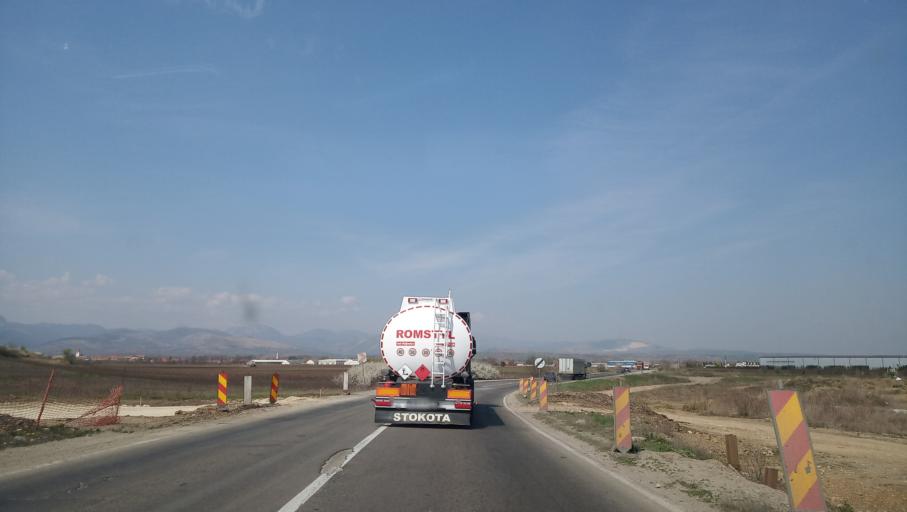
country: RO
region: Alba
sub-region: Comuna Santimbru
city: Santimbru
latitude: 46.1482
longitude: 23.6444
